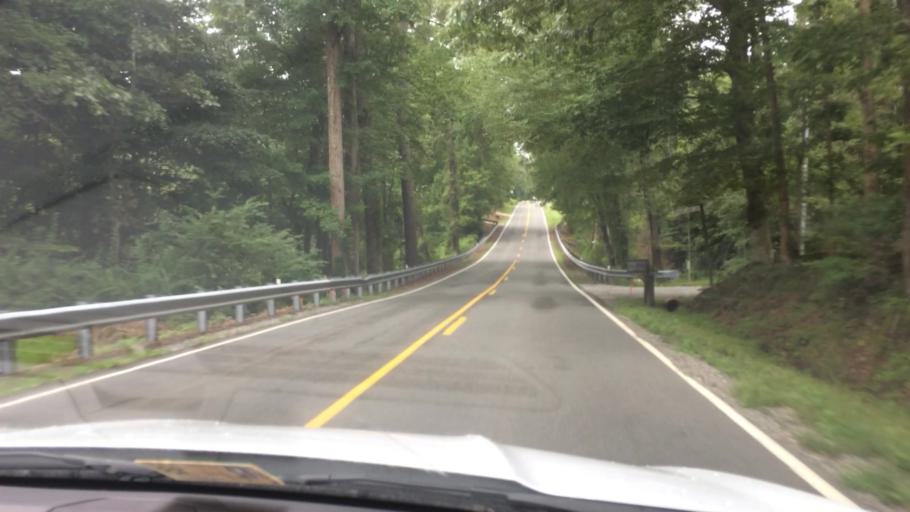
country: US
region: Virginia
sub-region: New Kent County
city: New Kent
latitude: 37.4557
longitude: -77.0363
